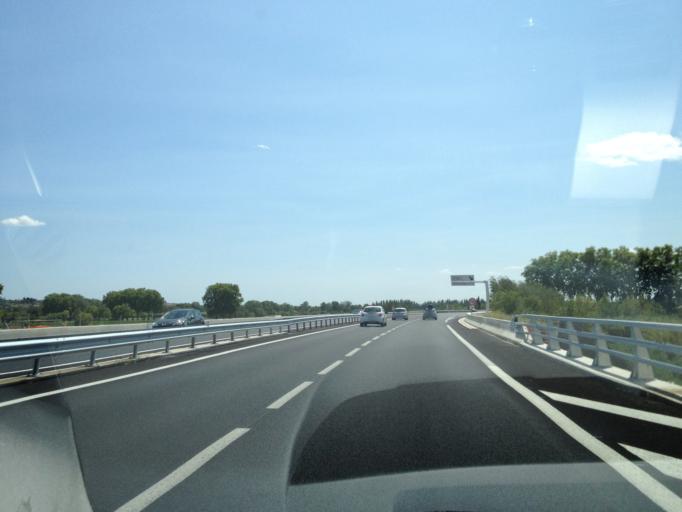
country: FR
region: Languedoc-Roussillon
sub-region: Departement de l'Herault
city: Pezenas
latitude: 43.4568
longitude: 3.4316
